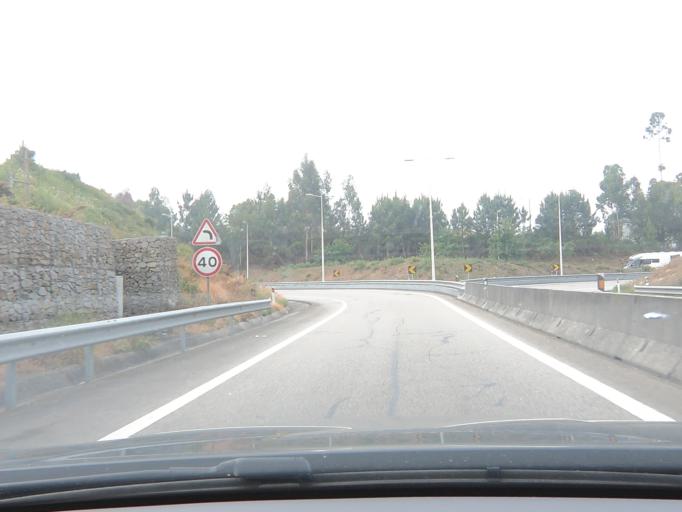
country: PT
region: Aveiro
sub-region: Santa Maria da Feira
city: Nogueira da Regedoura
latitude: 41.0117
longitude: -8.5853
